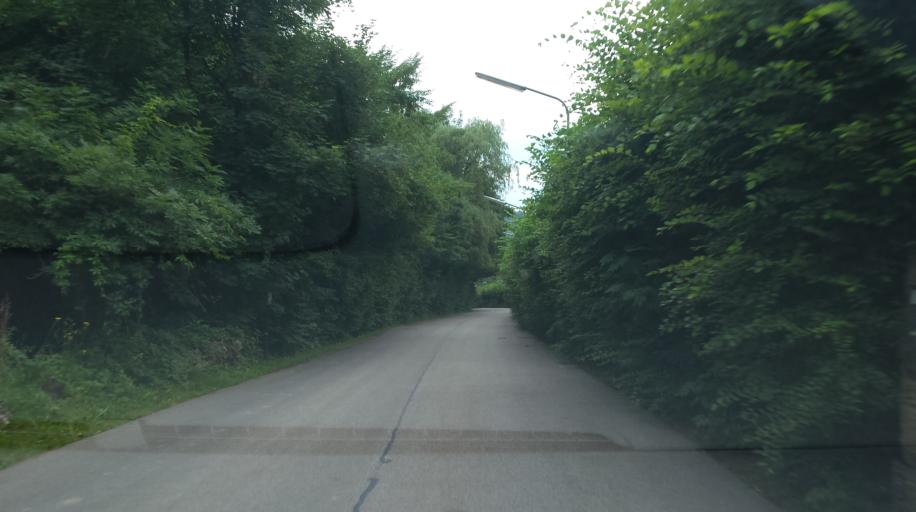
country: AT
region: Lower Austria
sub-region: Politischer Bezirk Wien-Umgebung
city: Mauerbach
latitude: 48.2411
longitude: 16.2069
